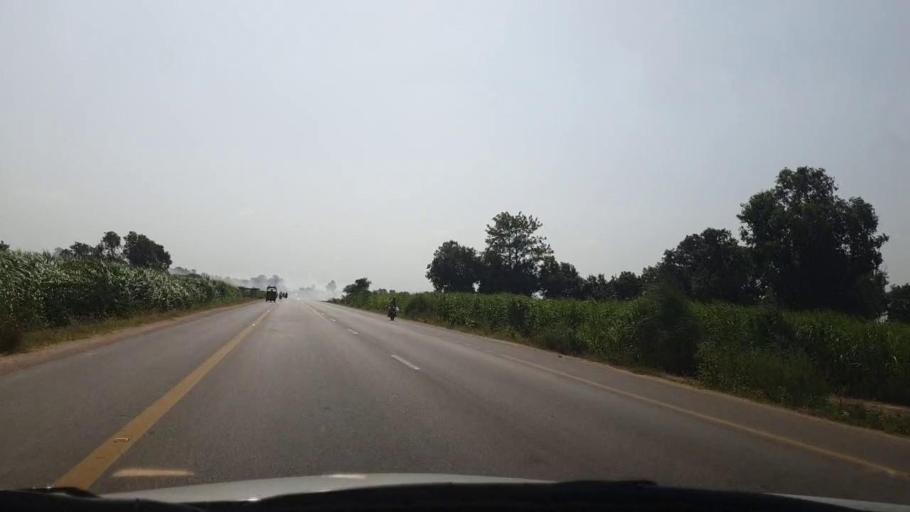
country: PK
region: Sindh
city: Matli
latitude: 25.0771
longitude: 68.6151
